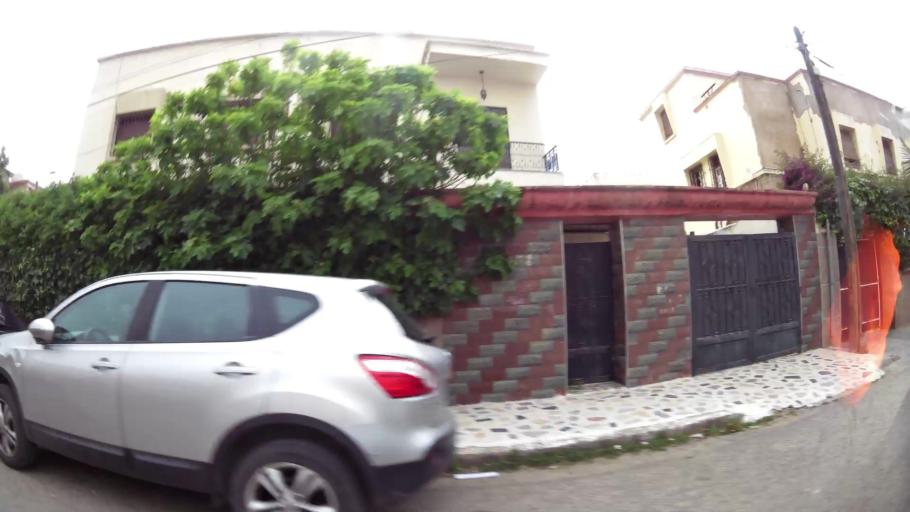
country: MA
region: Grand Casablanca
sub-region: Casablanca
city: Casablanca
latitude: 33.5680
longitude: -7.6121
